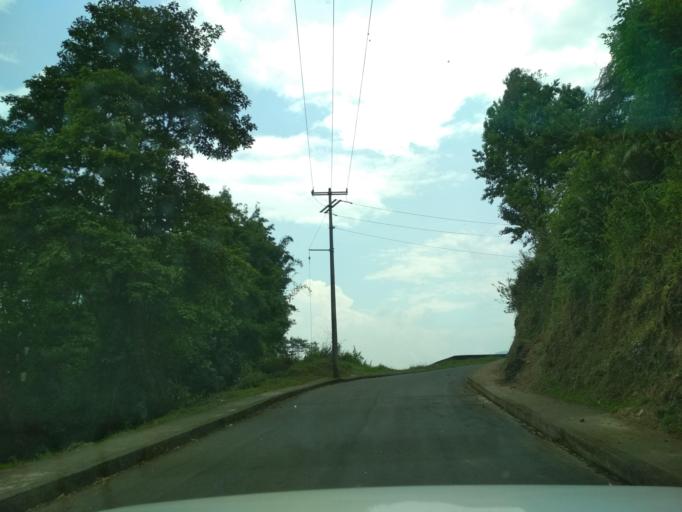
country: MX
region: Veracruz
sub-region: Mariano Escobedo
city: Mariano Escobedo
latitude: 18.9151
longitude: -97.1340
